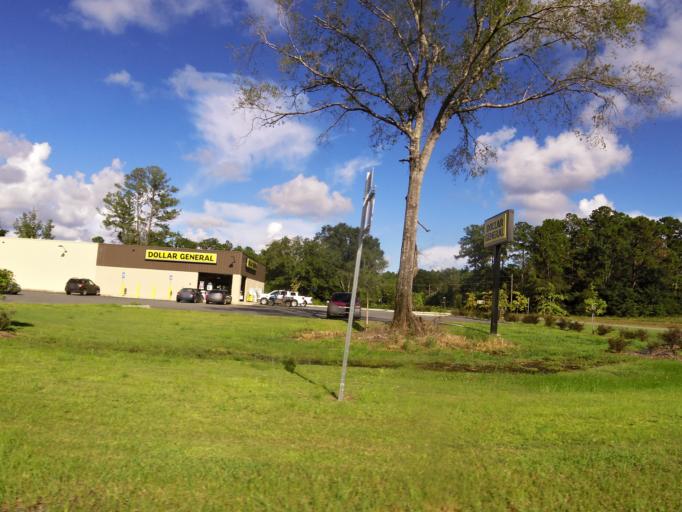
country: US
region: Georgia
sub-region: Camden County
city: Woodbine
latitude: 31.0943
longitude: -81.7258
